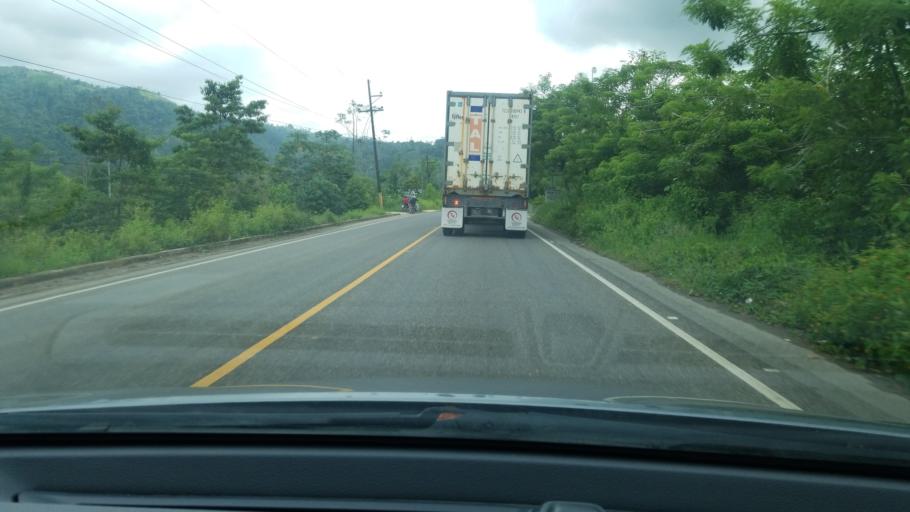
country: HN
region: Cortes
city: Potrerillos
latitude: 15.5902
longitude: -88.3269
